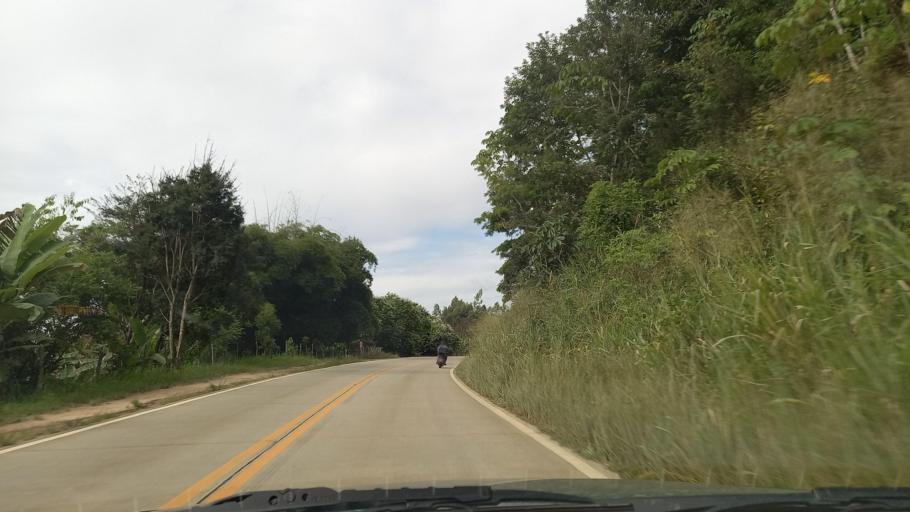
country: BR
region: Pernambuco
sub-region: Maraial
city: Maraial
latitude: -8.7484
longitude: -35.8171
